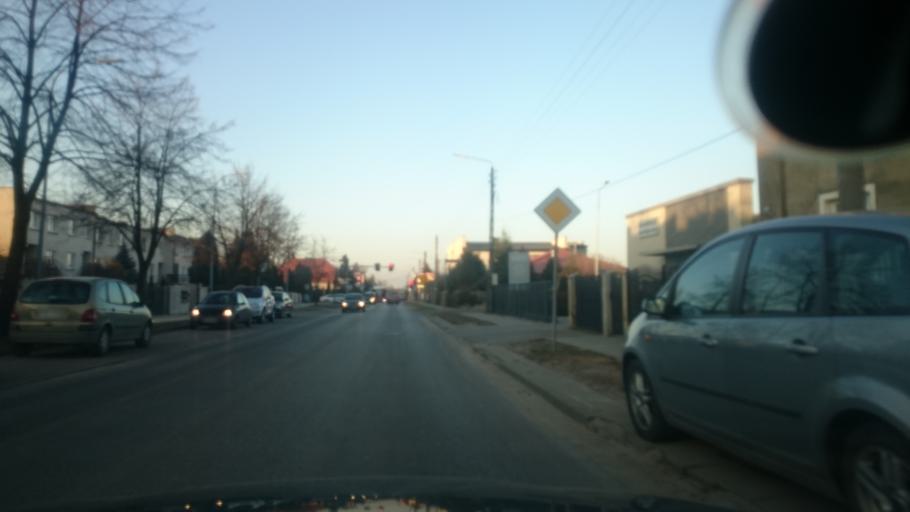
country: PL
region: Greater Poland Voivodeship
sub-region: Powiat ostrowski
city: Ostrow Wielkopolski
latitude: 51.6460
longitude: 17.8369
